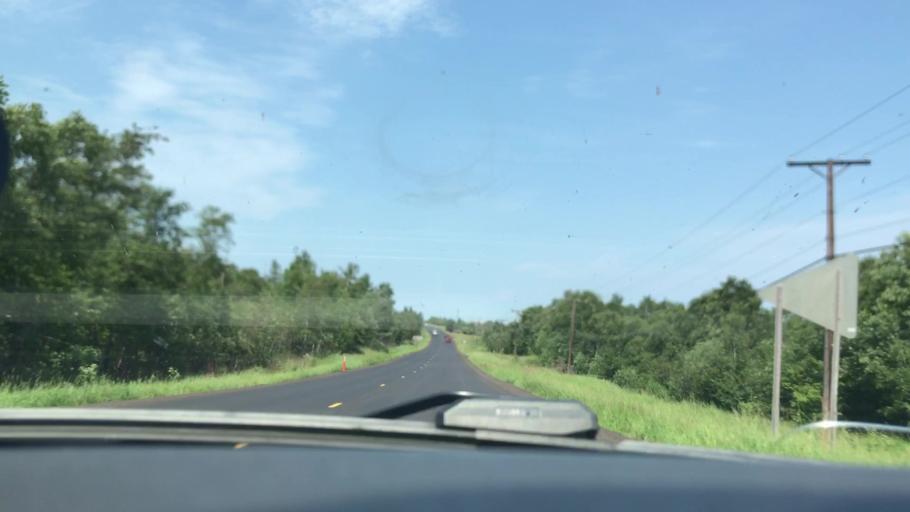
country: US
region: Minnesota
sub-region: Lake County
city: Silver Bay
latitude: 47.2760
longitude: -91.2745
